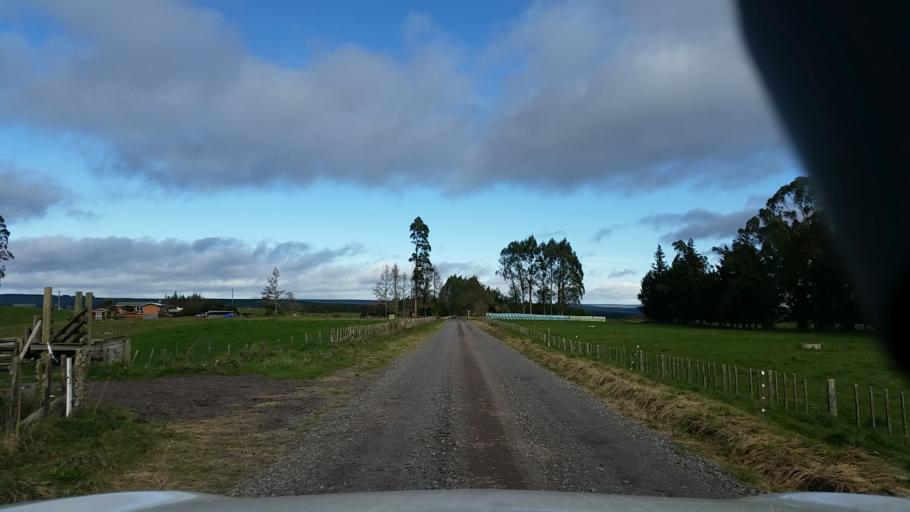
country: NZ
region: Bay of Plenty
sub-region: Whakatane District
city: Murupara
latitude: -38.4774
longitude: 176.4150
